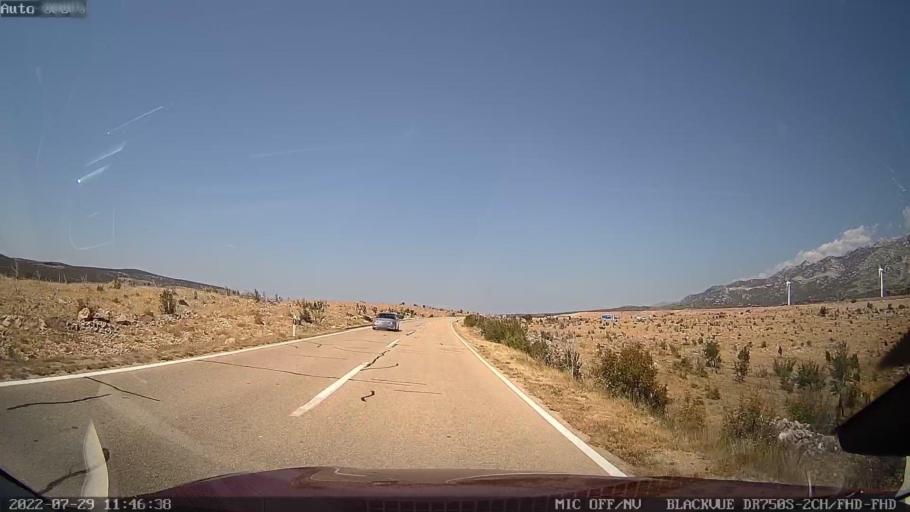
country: HR
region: Zadarska
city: Obrovac
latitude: 44.2190
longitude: 15.6595
